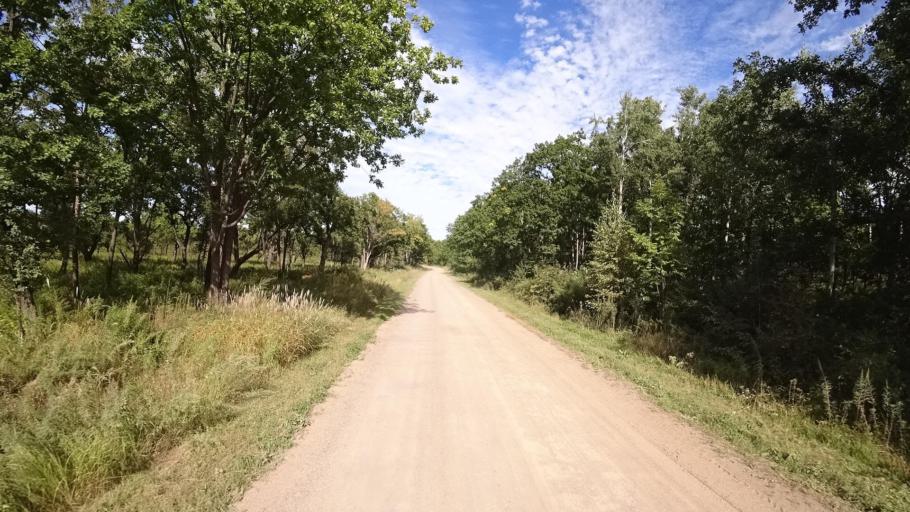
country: RU
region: Primorskiy
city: Yakovlevka
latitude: 44.3963
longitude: 133.5592
